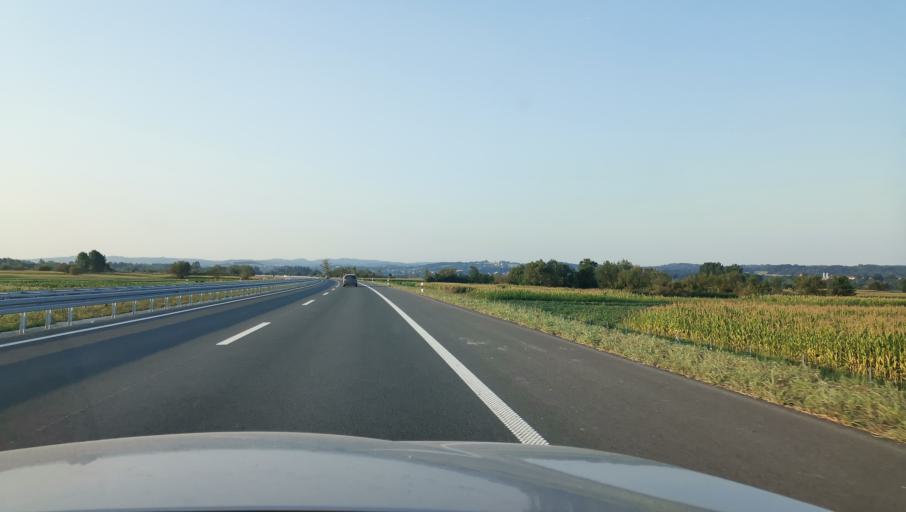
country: RS
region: Central Serbia
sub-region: Kolubarski Okrug
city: Ljig
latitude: 44.2521
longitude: 20.2697
